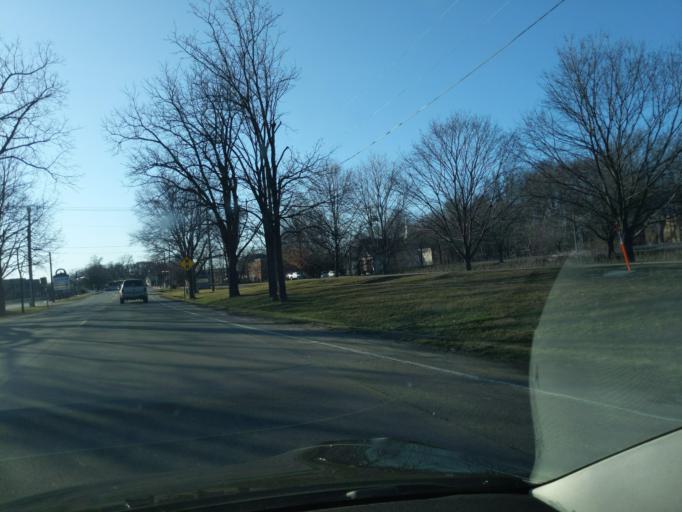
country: US
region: Michigan
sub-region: Washtenaw County
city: Chelsea
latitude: 42.3061
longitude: -84.0184
